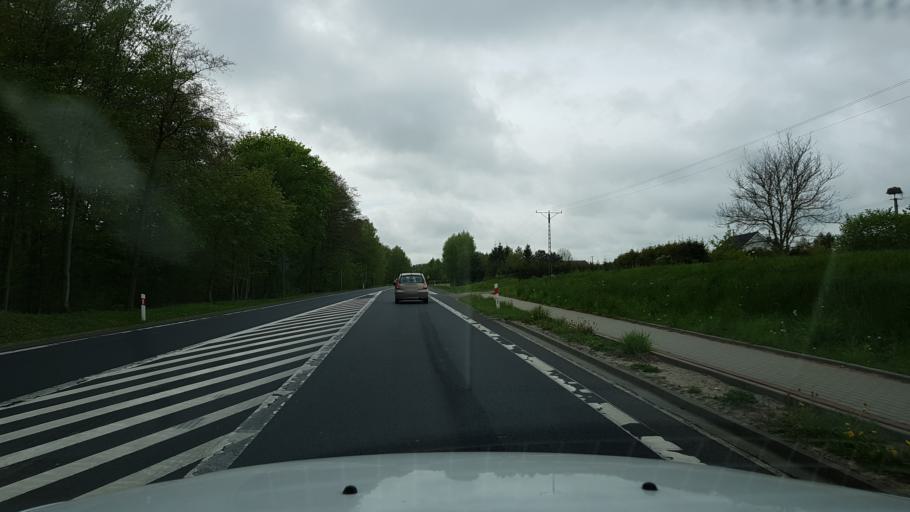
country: PL
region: West Pomeranian Voivodeship
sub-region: Powiat slawienski
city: Darlowo
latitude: 54.2774
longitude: 16.4727
